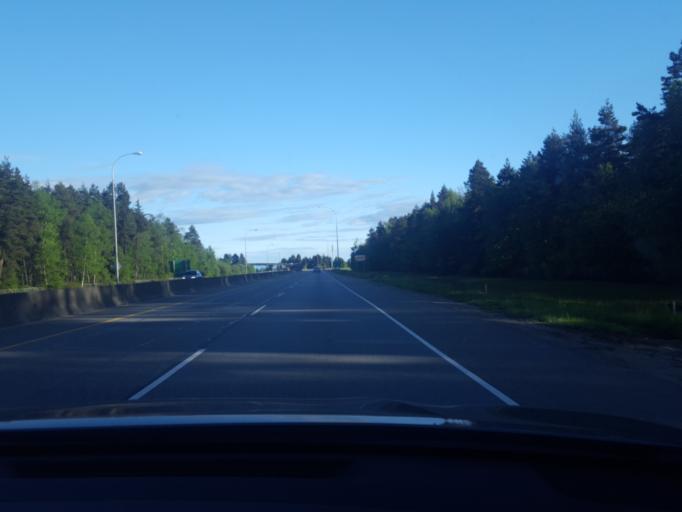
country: CA
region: British Columbia
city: Delta
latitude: 49.1264
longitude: -122.9282
